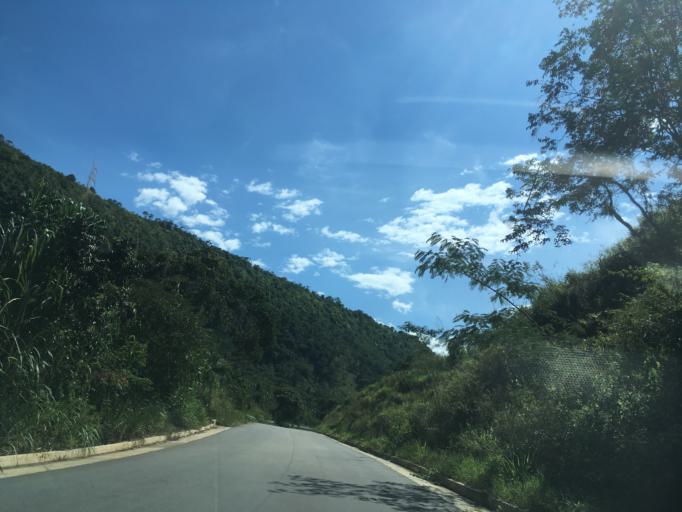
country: CO
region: Santander
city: Coromoro
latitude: 6.3040
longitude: -73.1438
